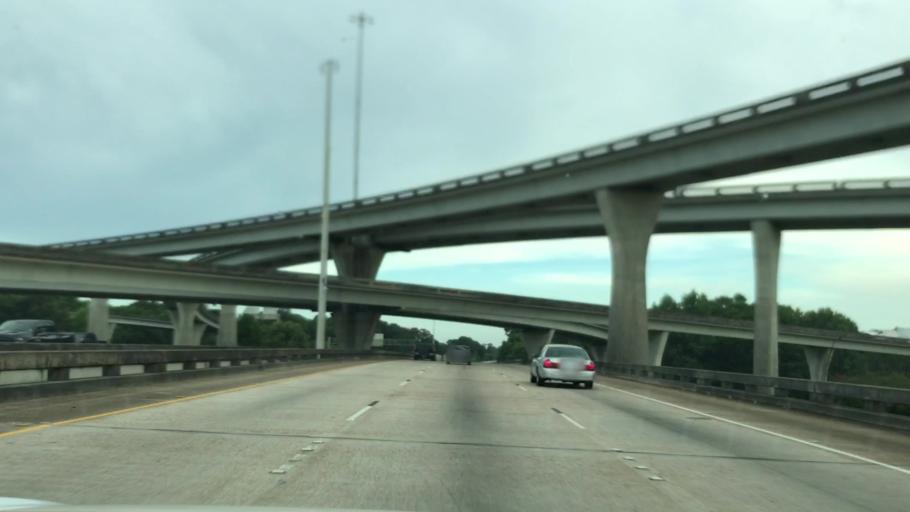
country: US
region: Louisiana
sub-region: East Baton Rouge Parish
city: Merrydale
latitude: 30.5098
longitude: -91.1587
